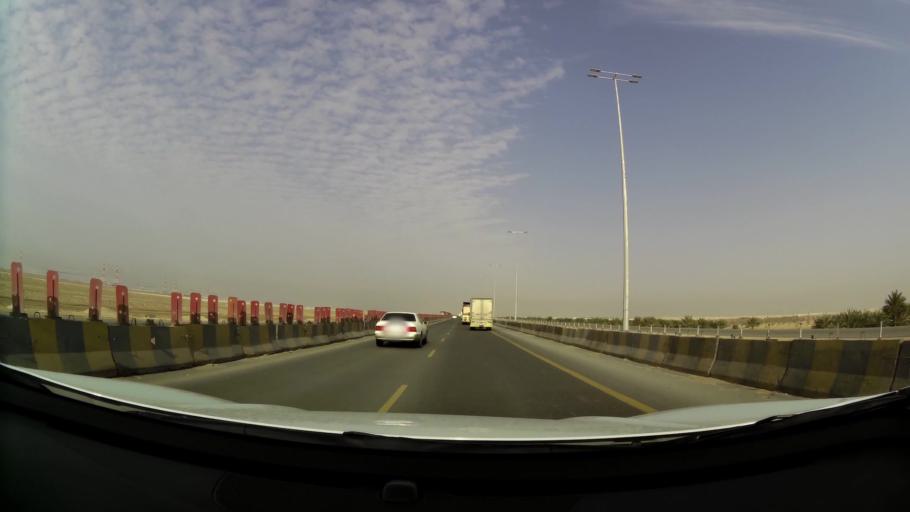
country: AE
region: Abu Dhabi
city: Abu Dhabi
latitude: 24.2250
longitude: 54.4412
